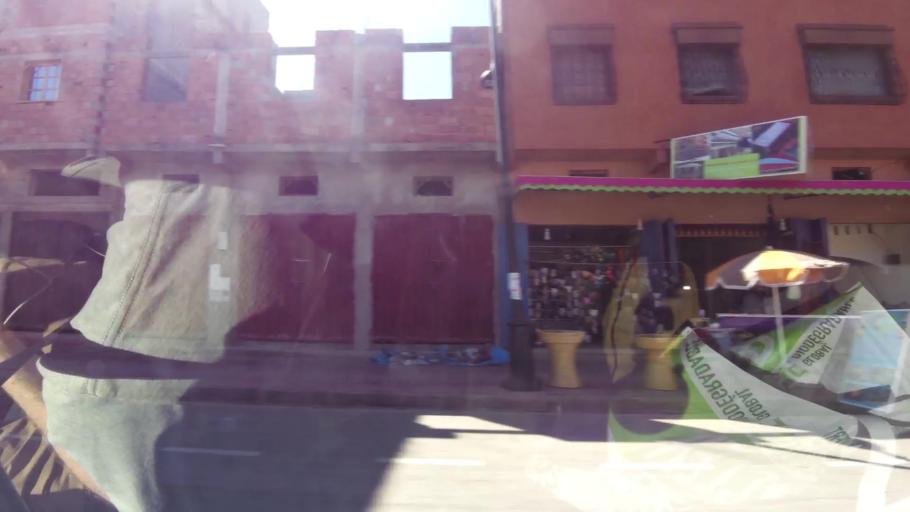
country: MA
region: Marrakech-Tensift-Al Haouz
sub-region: Marrakech
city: Marrakesh
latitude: 31.5887
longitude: -8.0575
